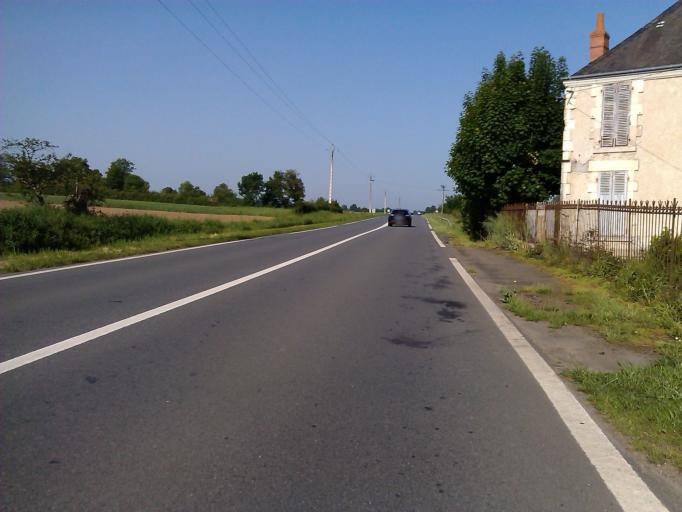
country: FR
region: Centre
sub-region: Departement de l'Indre
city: Neuvy-Saint-Sepulchre
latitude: 46.5741
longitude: 1.8875
